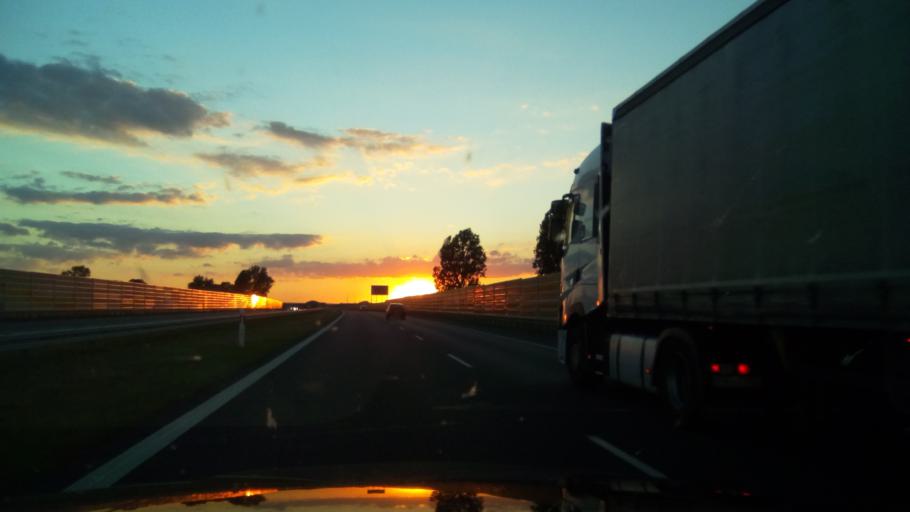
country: PL
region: Lodz Voivodeship
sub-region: Powiat poddebicki
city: Wartkowice
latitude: 51.9899
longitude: 19.0550
